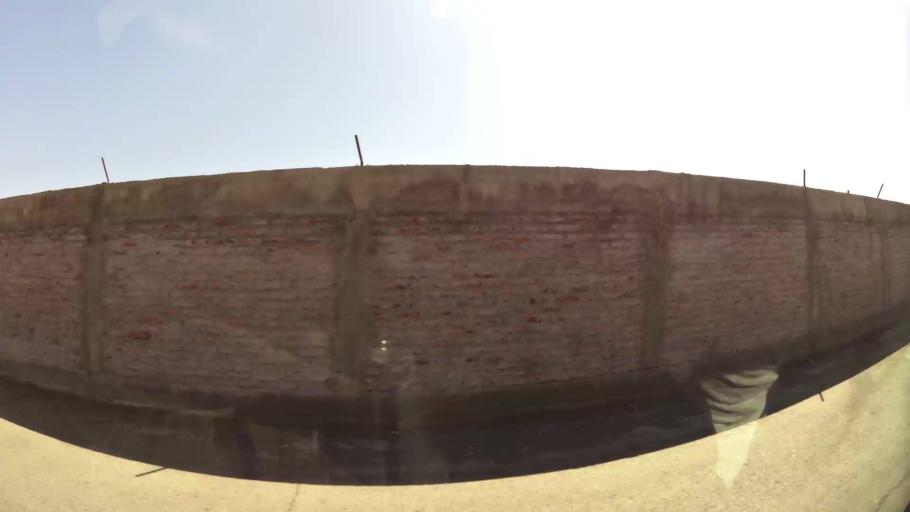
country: CL
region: Santiago Metropolitan
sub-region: Provincia de Santiago
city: Lo Prado
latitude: -33.3776
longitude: -70.7439
